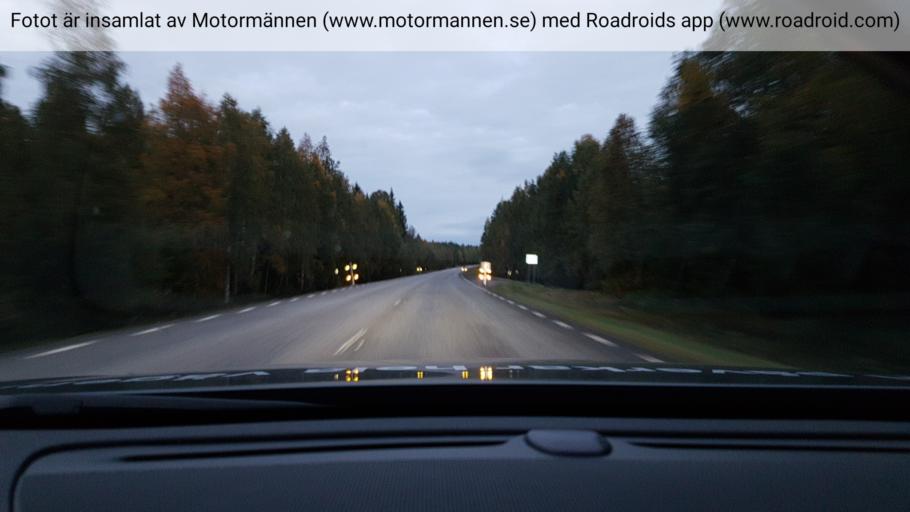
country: SE
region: Norrbotten
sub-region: Alvsbyns Kommun
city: AElvsbyn
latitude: 65.7817
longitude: 20.8113
